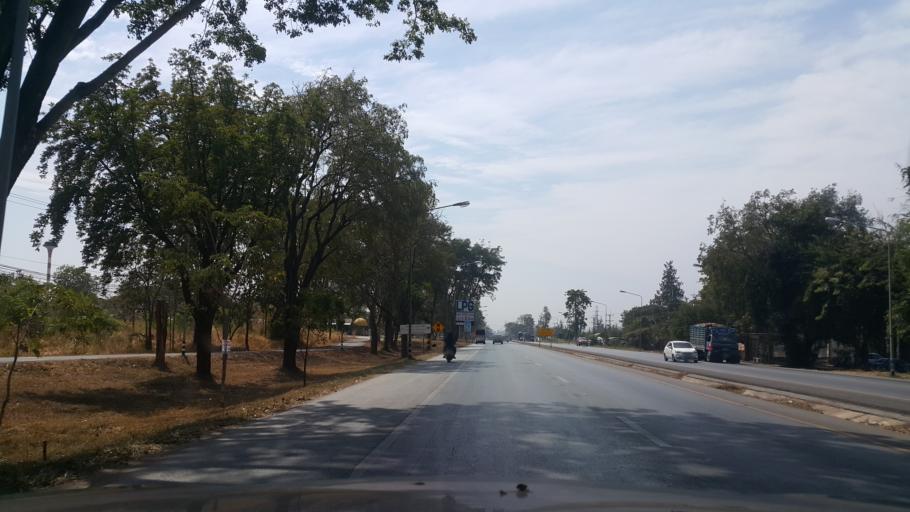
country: TH
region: Nakhon Ratchasima
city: Nakhon Ratchasima
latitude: 14.8617
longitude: 102.0700
